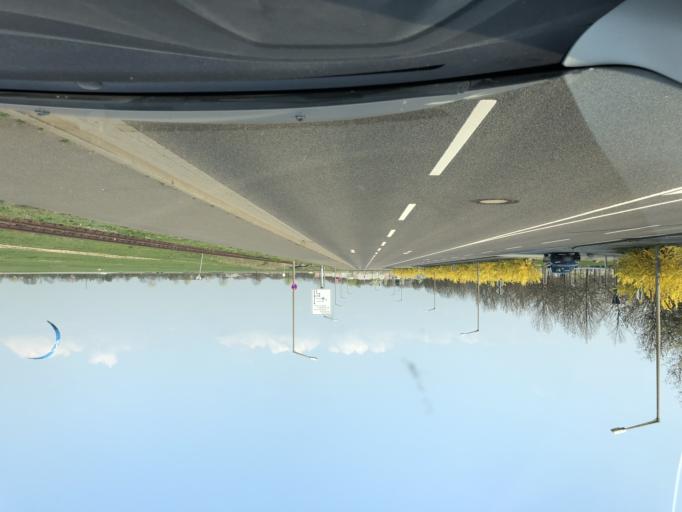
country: DE
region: Saxony
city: Rackwitz
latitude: 51.3959
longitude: 12.4130
